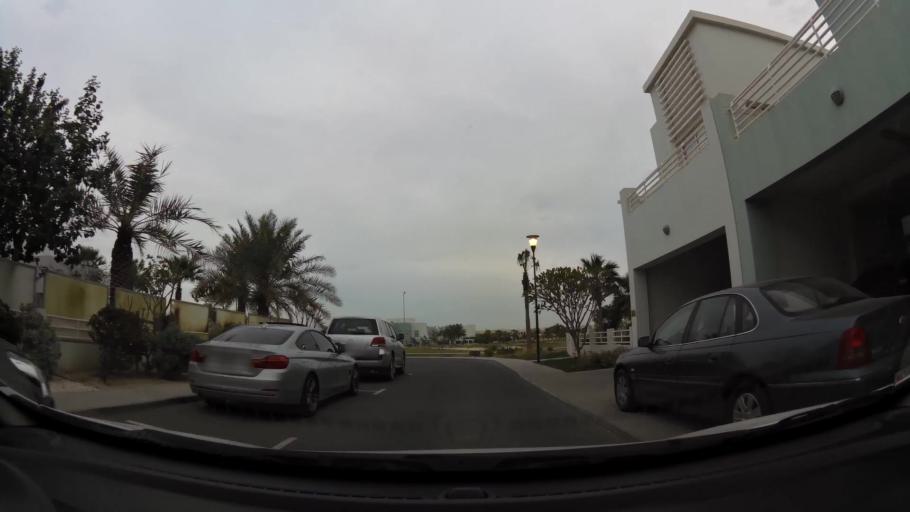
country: BH
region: Northern
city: Ar Rifa'
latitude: 26.0996
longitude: 50.5638
